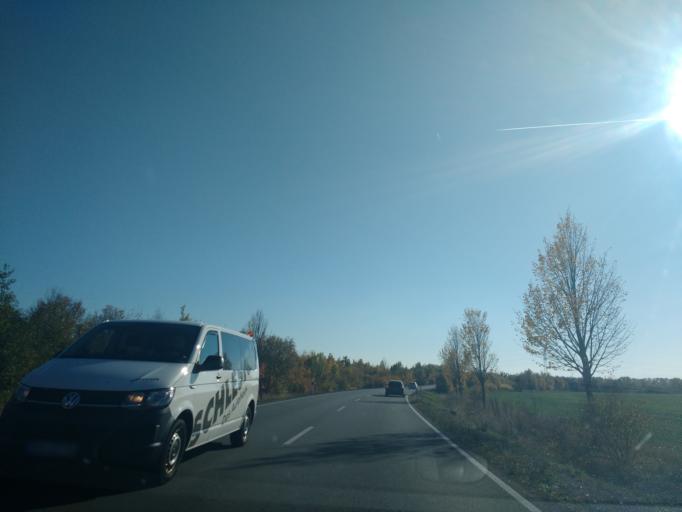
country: DE
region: Saxony-Anhalt
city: Sangerhausen
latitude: 51.4523
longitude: 11.2629
